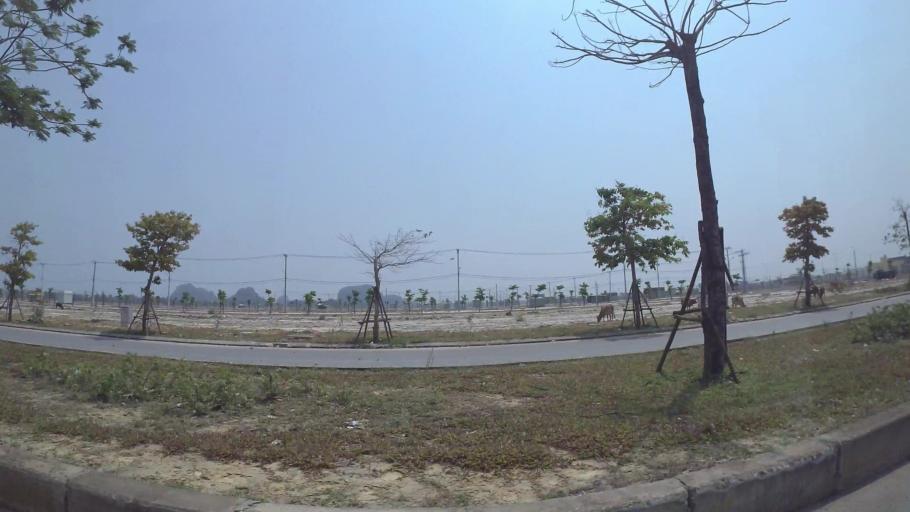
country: VN
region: Da Nang
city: Ngu Hanh Son
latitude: 16.0108
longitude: 108.2436
